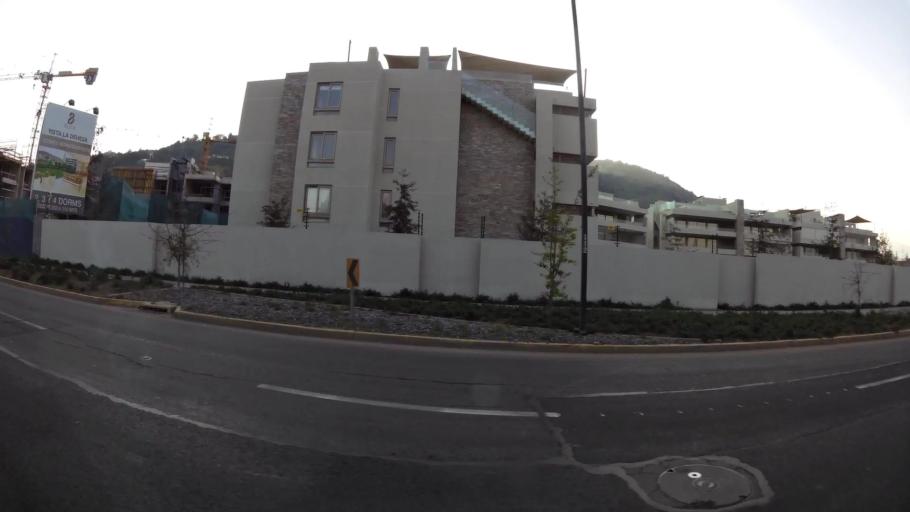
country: CL
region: Santiago Metropolitan
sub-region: Provincia de Santiago
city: Villa Presidente Frei, Nunoa, Santiago, Chile
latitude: -33.3594
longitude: -70.5440
